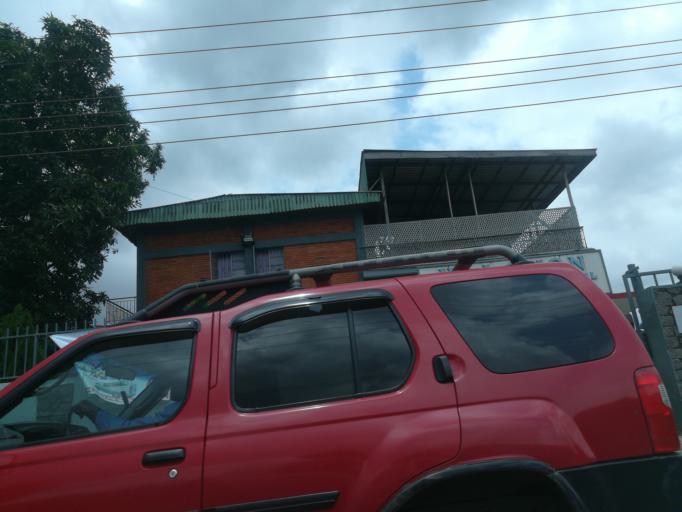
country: NG
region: Lagos
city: Somolu
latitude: 6.5507
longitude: 3.3619
